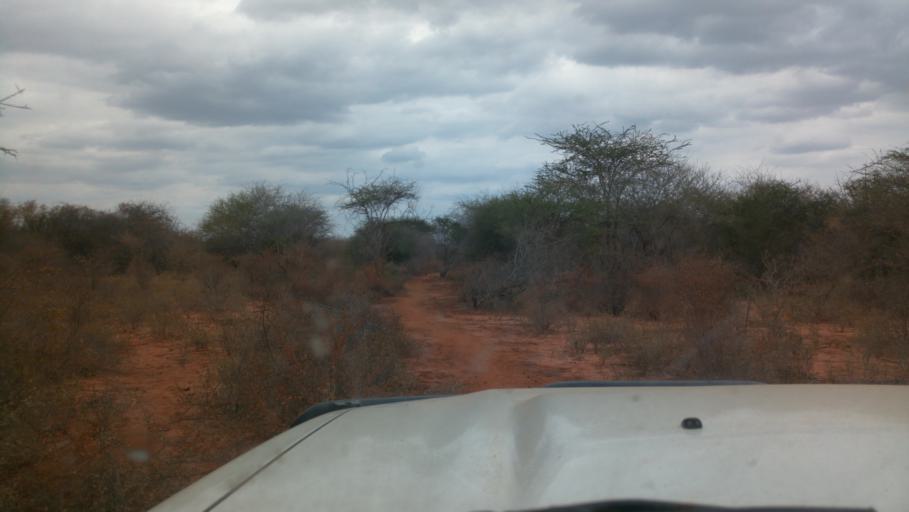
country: KE
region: Kitui
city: Kitui
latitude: -1.7746
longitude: 38.4594
